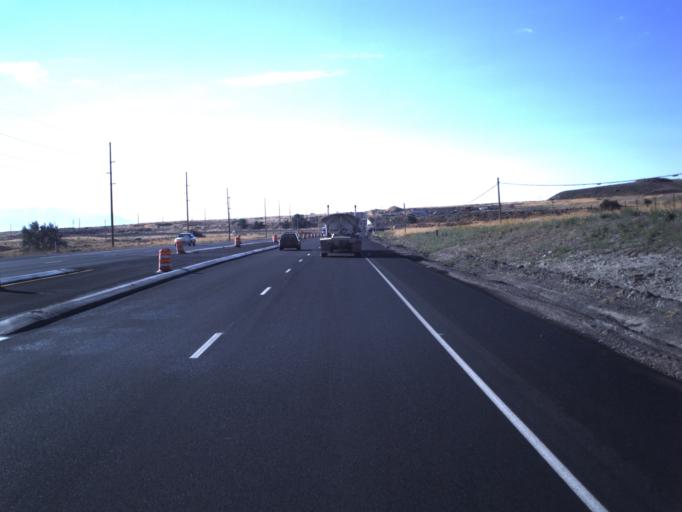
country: US
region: Utah
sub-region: Salt Lake County
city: Oquirrh
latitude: 40.6573
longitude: -112.0798
